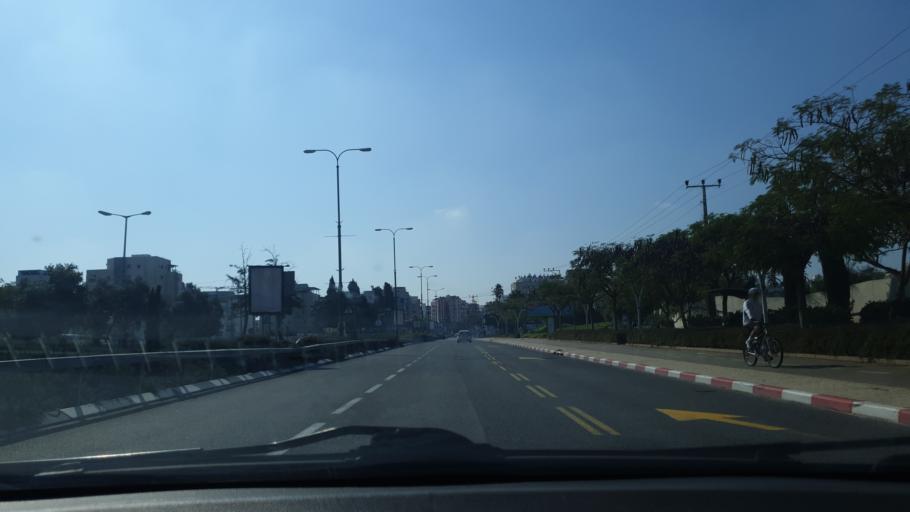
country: IL
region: Central District
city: Rishon LeZiyyon
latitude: 31.9760
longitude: 34.8074
